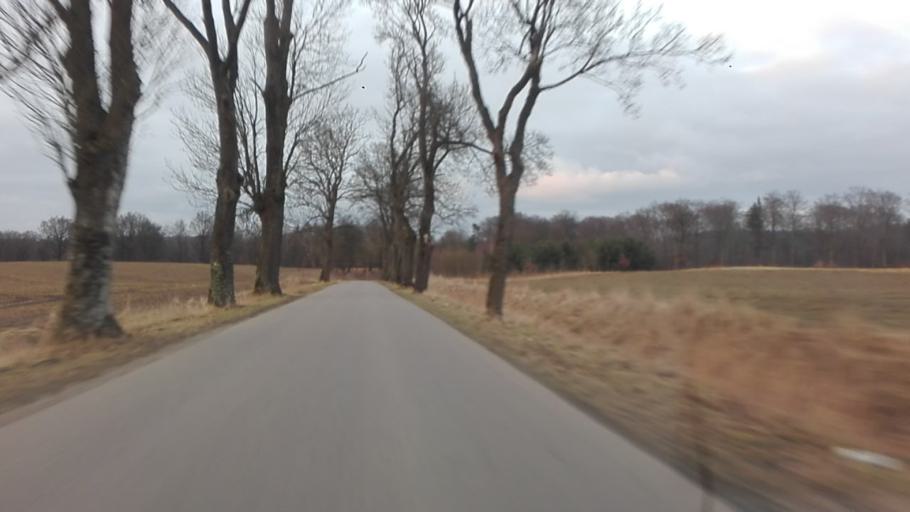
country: PL
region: West Pomeranian Voivodeship
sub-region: Powiat swidwinski
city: Rabino
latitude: 53.8284
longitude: 15.9302
